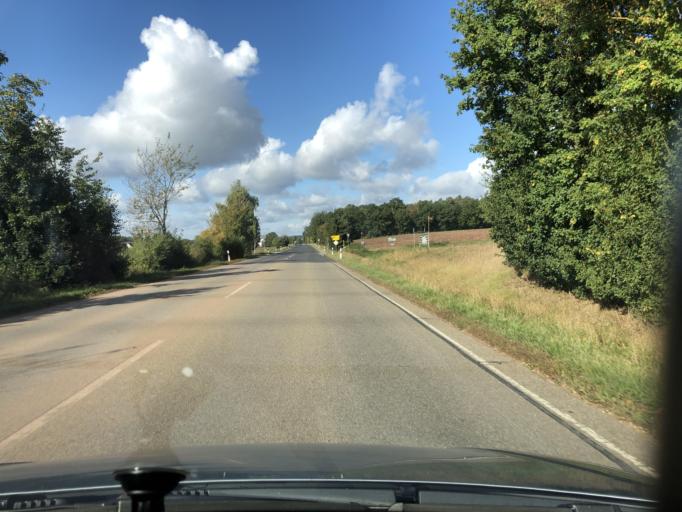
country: DE
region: Bavaria
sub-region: Regierungsbezirk Mittelfranken
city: Puschendorf
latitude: 49.4928
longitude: 10.8324
